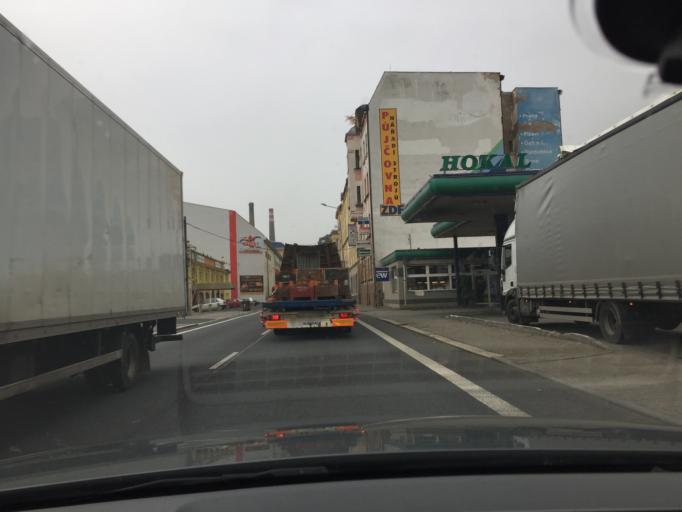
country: CZ
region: Ustecky
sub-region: Okres Usti nad Labem
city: Usti nad Labem
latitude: 50.6503
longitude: 14.0421
